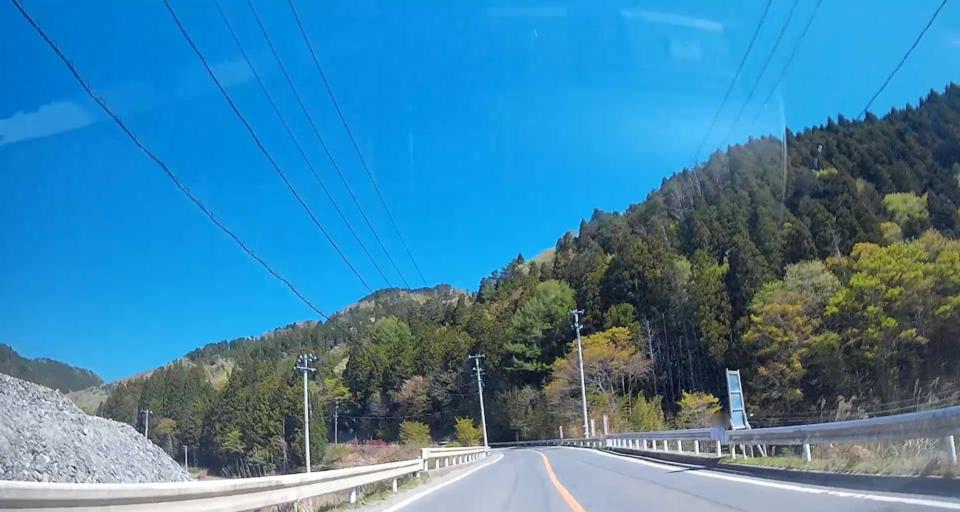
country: JP
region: Miyagi
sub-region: Oshika Gun
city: Onagawa Cho
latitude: 38.5124
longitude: 141.4555
